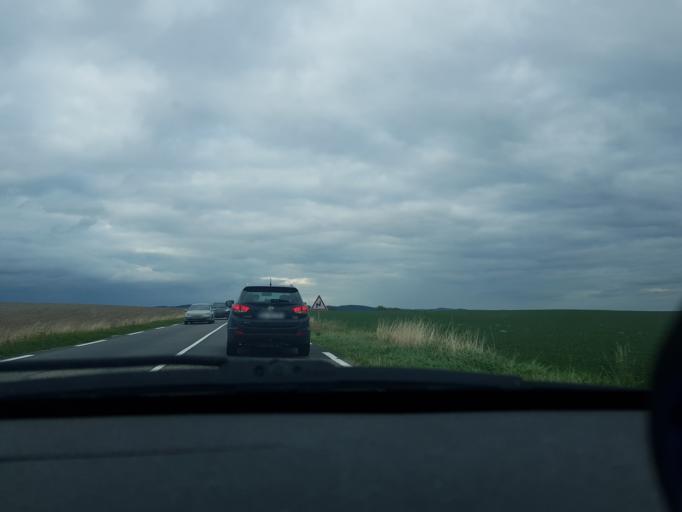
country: FR
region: Lorraine
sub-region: Departement de la Moselle
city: Morhange
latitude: 48.9290
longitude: 6.6013
